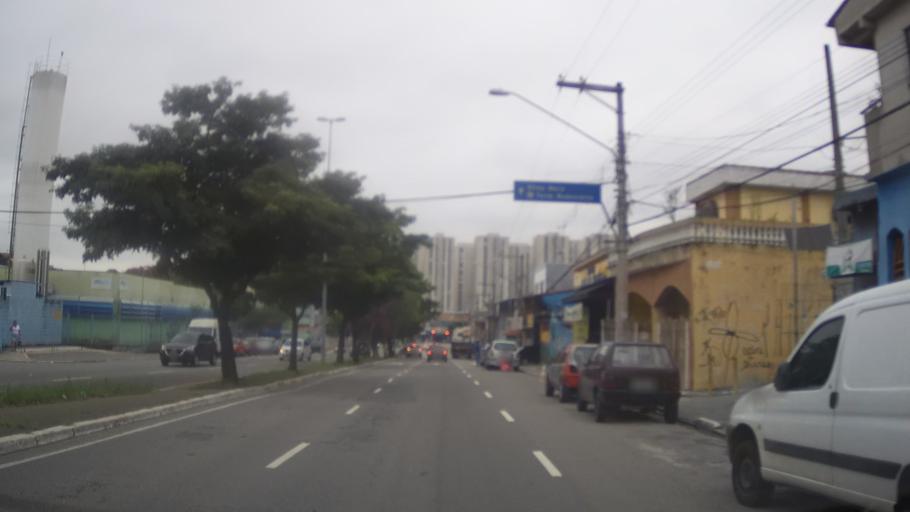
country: BR
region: Sao Paulo
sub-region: Guarulhos
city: Guarulhos
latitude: -23.4366
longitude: -46.5495
